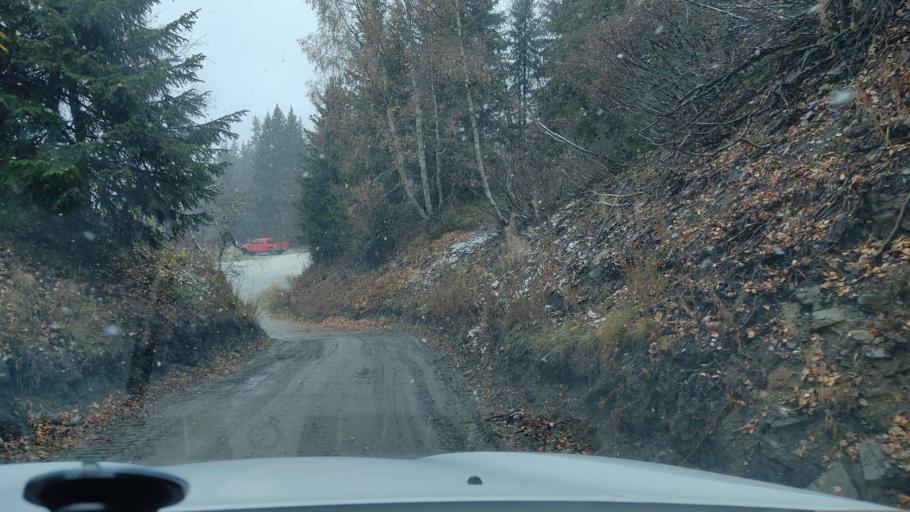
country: FR
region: Rhone-Alpes
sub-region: Departement de la Savoie
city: Bourg-Saint-Maurice
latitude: 45.5763
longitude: 6.7900
